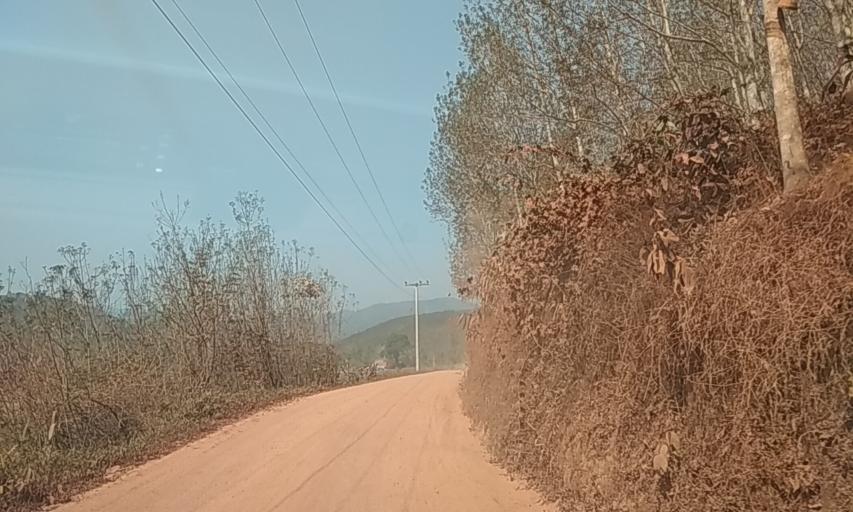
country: CN
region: Yunnan
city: Mengla
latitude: 21.5156
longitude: 101.8508
